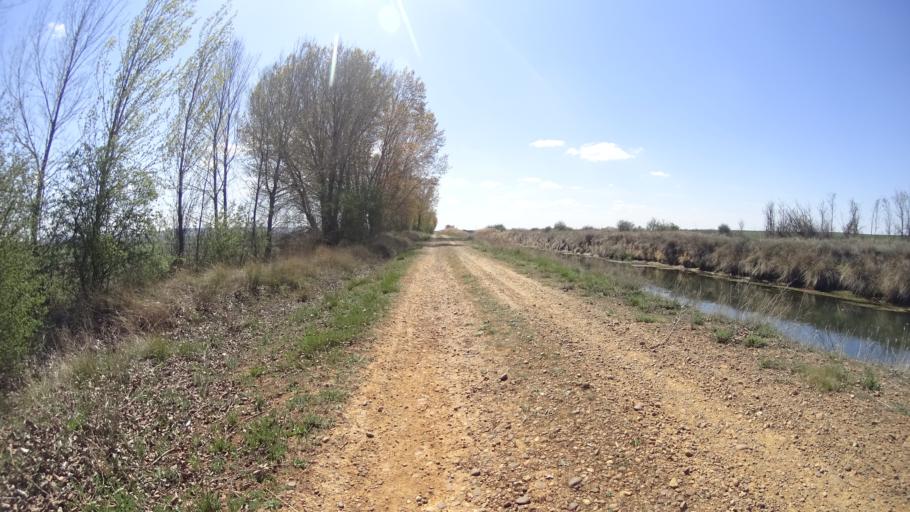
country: ES
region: Castille and Leon
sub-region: Provincia de Palencia
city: Grijota
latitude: 42.0807
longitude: -4.5783
